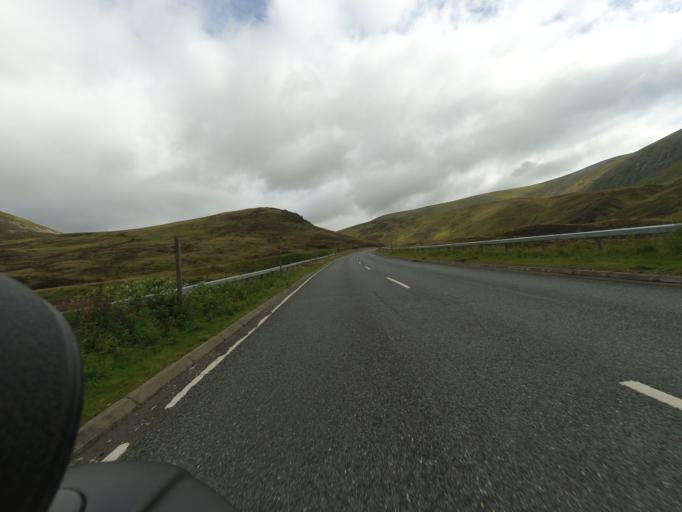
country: GB
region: Scotland
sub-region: Perth and Kinross
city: Blairgowrie
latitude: 56.8628
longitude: -3.4213
